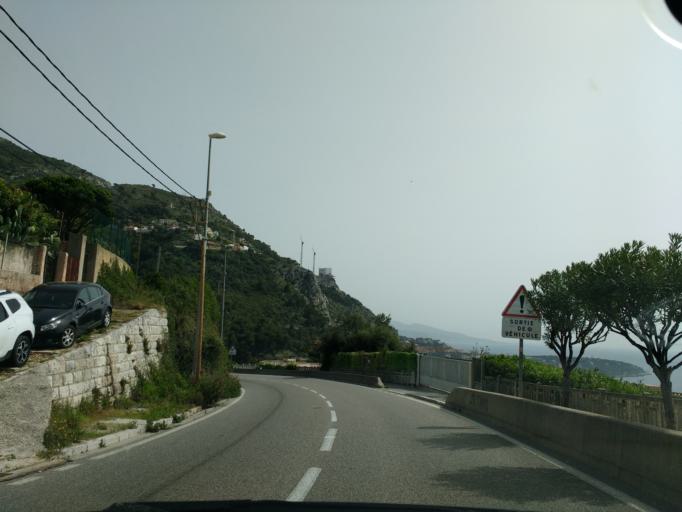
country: MC
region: Commune de Monaco
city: Saint-Roman
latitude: 43.7518
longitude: 7.4315
